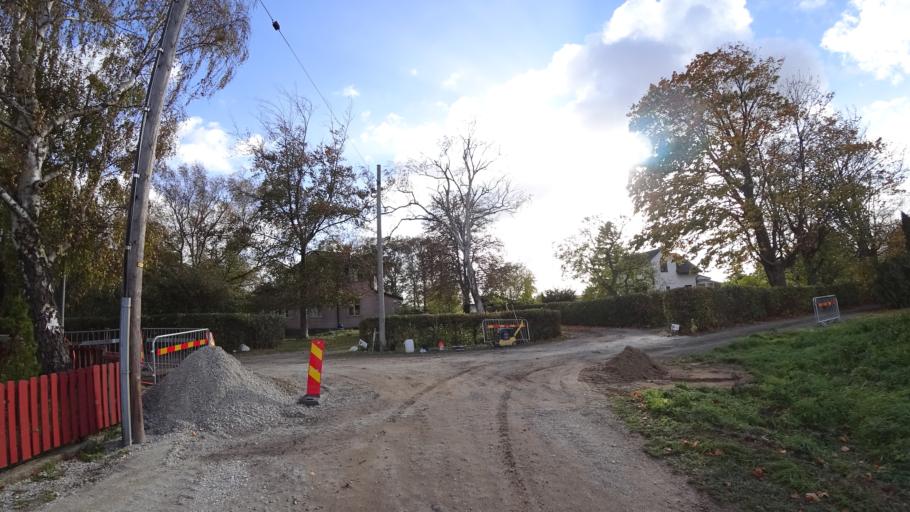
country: SE
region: Skane
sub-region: Staffanstorps Kommun
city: Hjaerup
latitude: 55.6217
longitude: 13.1227
